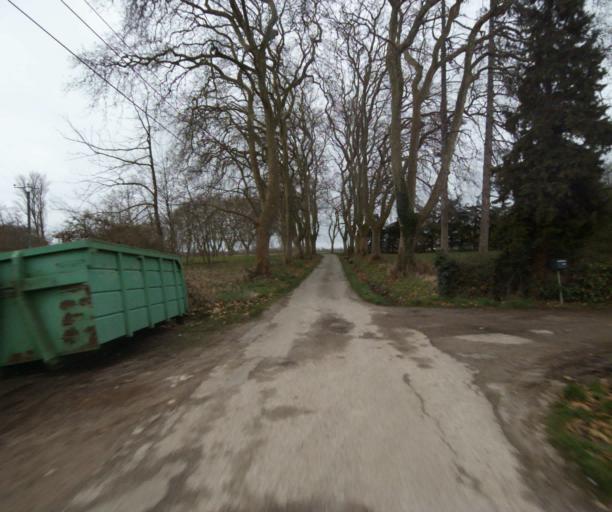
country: FR
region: Midi-Pyrenees
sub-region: Departement de l'Ariege
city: Saverdun
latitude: 43.2206
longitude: 1.5883
